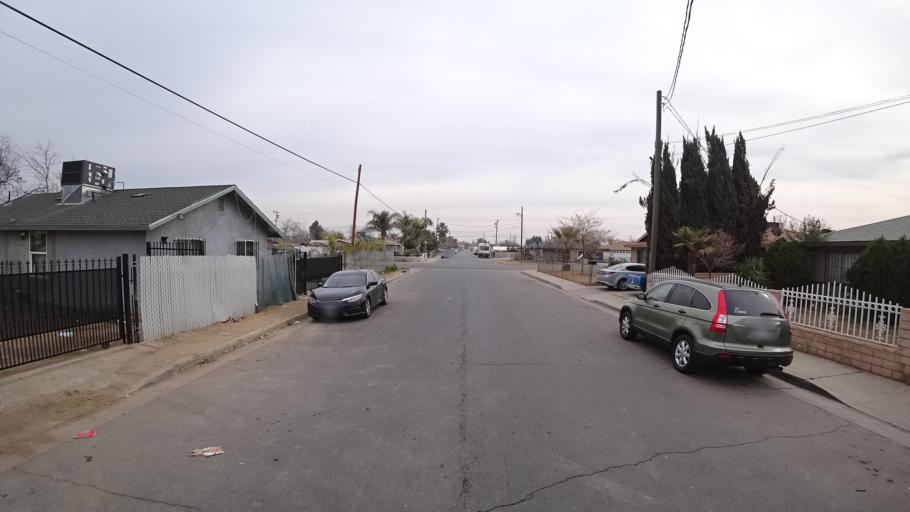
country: US
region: California
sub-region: Kern County
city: Bakersfield
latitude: 35.3662
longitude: -118.9832
